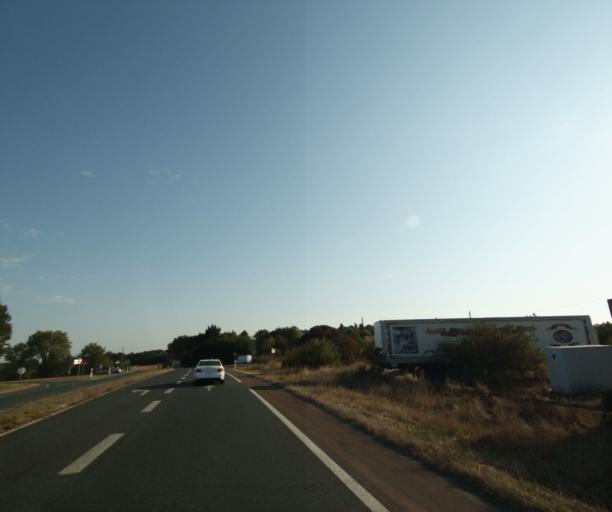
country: FR
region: Poitou-Charentes
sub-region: Departement de la Charente-Maritime
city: Cabariot
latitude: 45.9343
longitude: -0.8660
